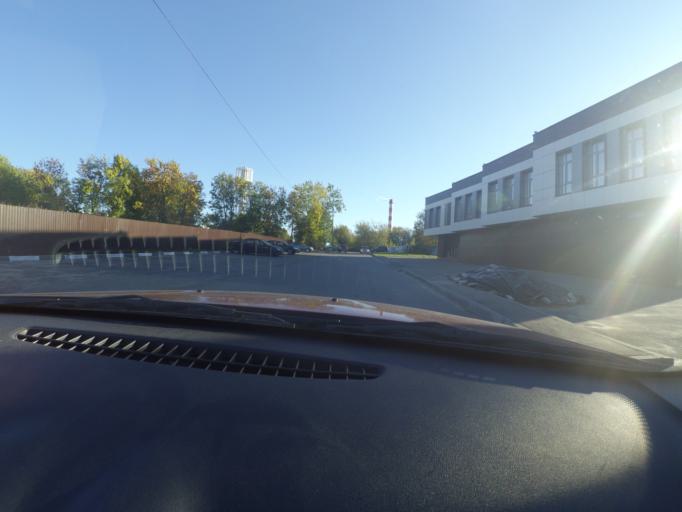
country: RU
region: Nizjnij Novgorod
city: Bor
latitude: 56.3084
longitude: 44.0706
